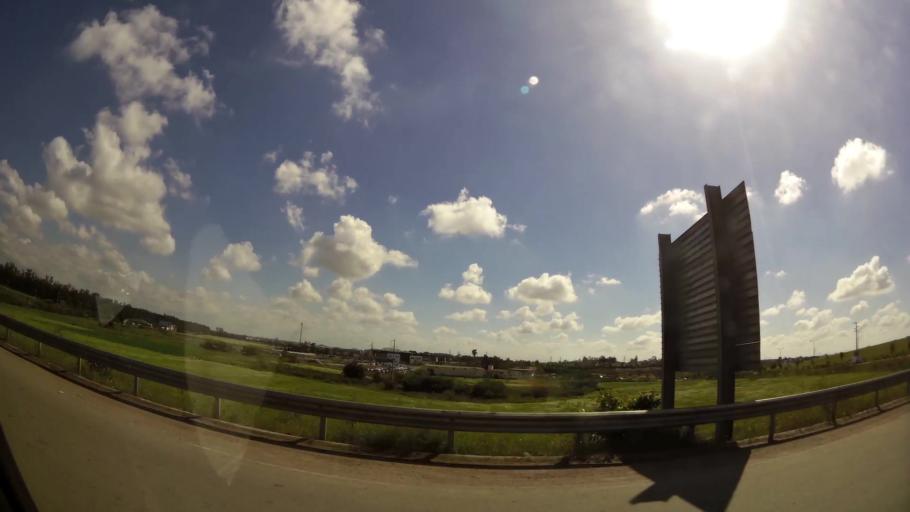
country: MA
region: Grand Casablanca
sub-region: Nouaceur
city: Bouskoura
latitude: 33.4847
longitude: -7.6352
